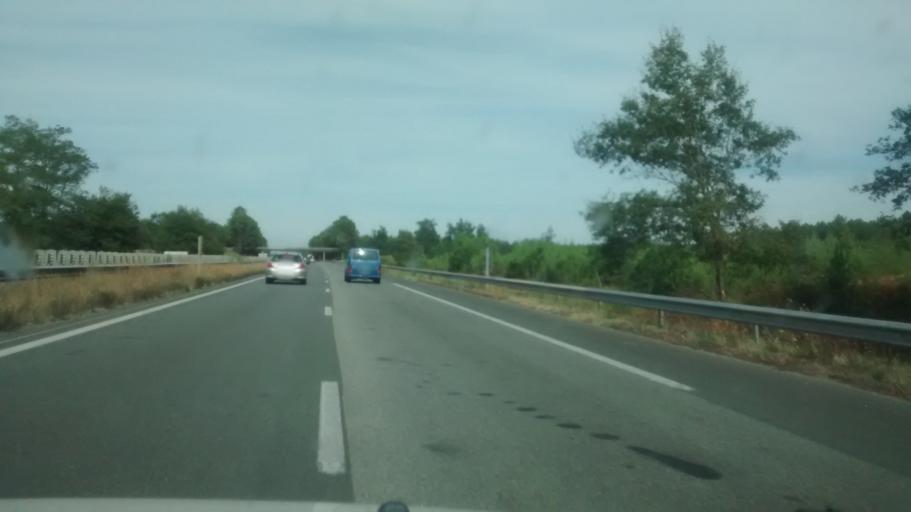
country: FR
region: Aquitaine
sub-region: Departement de la Gironde
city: Illats
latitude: 44.6192
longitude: -0.3872
